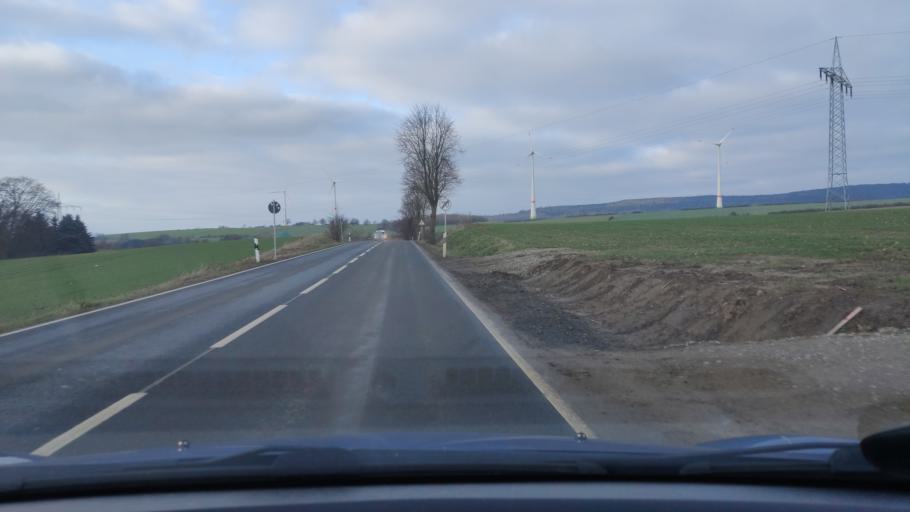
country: DE
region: Lower Saxony
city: Coppenbrugge
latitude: 52.1263
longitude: 9.5445
